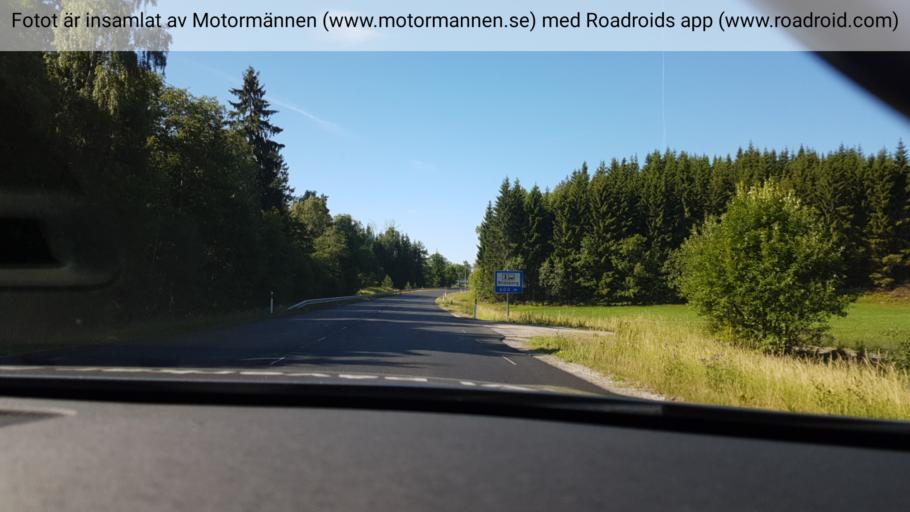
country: SE
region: Vaestra Goetaland
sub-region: Ulricehamns Kommun
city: Ulricehamn
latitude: 57.9418
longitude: 13.5107
